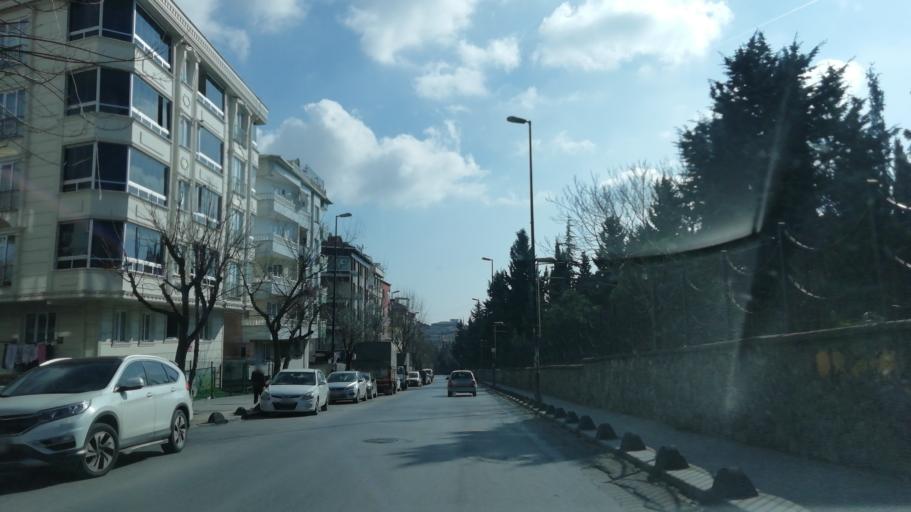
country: TR
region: Istanbul
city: Bahcelievler
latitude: 41.0174
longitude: 28.8359
